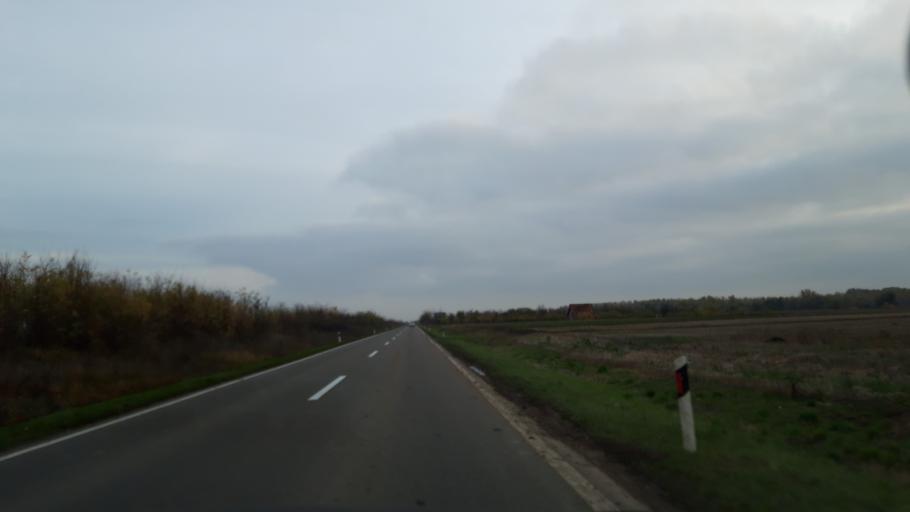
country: RS
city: Sanad
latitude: 45.9967
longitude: 20.1045
